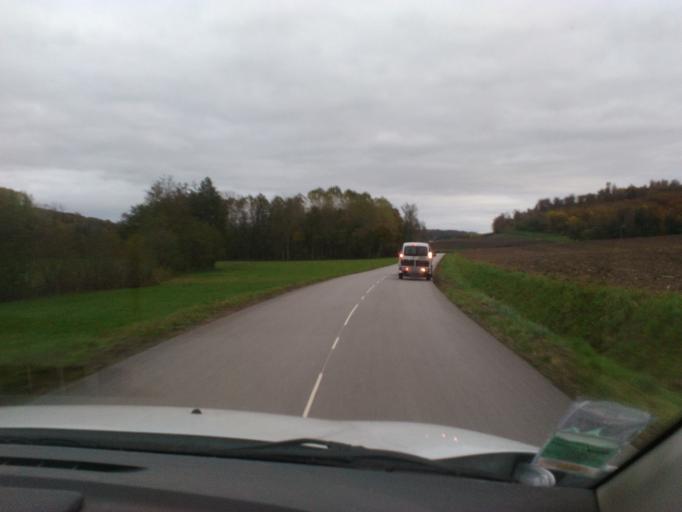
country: FR
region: Lorraine
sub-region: Departement des Vosges
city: Vincey
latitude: 48.2745
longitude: 6.2425
